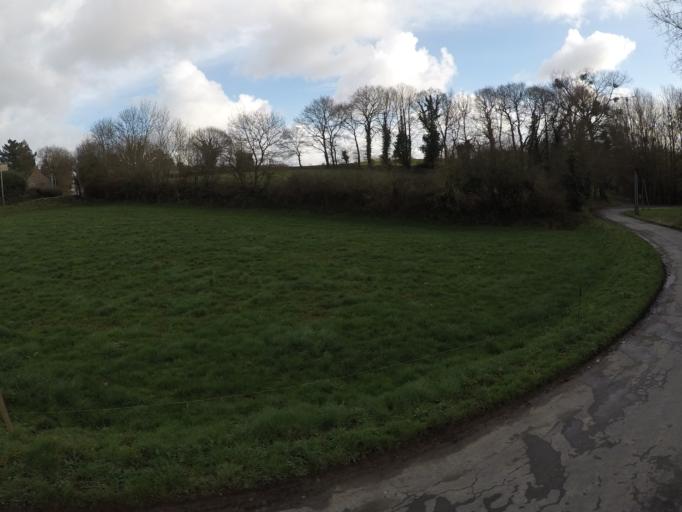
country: FR
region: Brittany
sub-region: Departement des Cotes-d'Armor
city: Lanvollon
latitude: 48.6160
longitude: -2.9884
